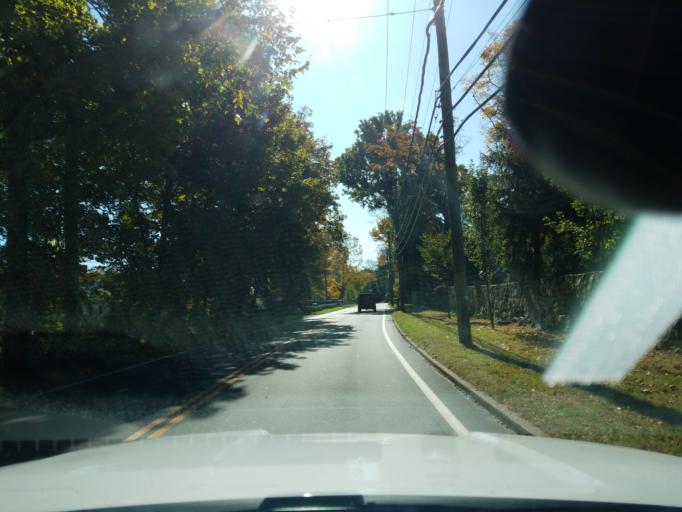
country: US
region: Connecticut
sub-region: Fairfield County
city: Greenwich
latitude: 41.0869
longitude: -73.6280
